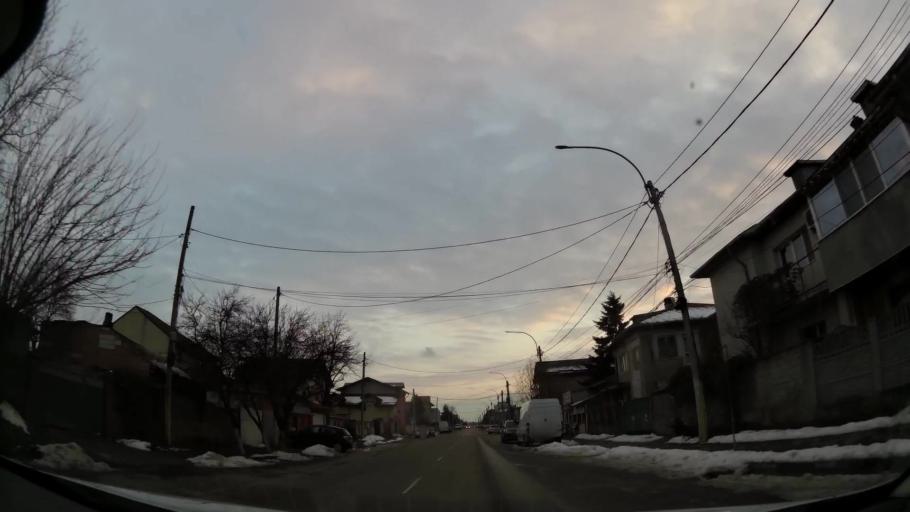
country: RO
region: Ilfov
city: Dobroesti
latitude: 44.4527
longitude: 26.1854
